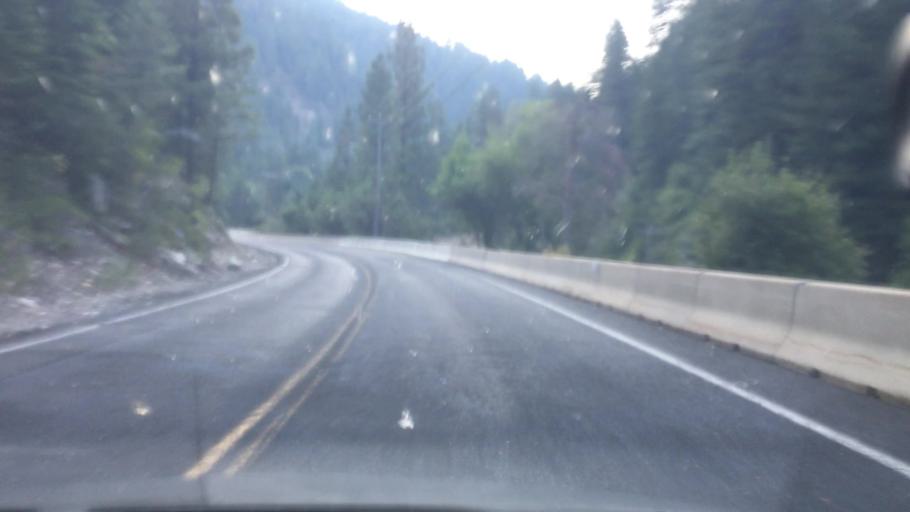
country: US
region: Idaho
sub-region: Valley County
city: McCall
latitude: 45.1375
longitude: -116.2837
